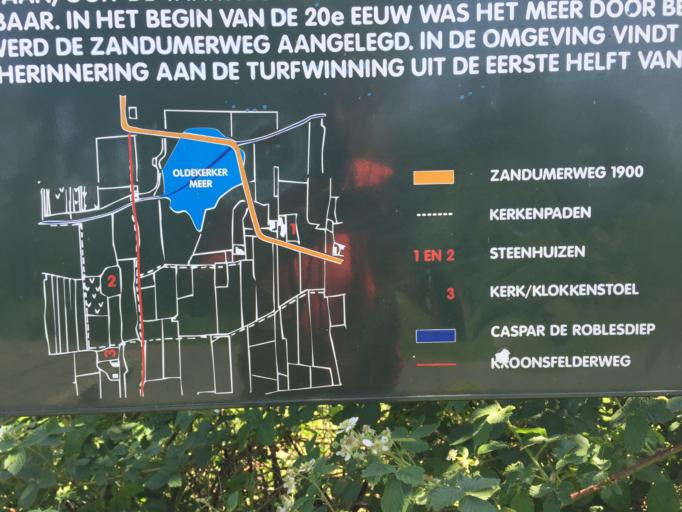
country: NL
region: Groningen
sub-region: Gemeente Zuidhorn
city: Grijpskerk
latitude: 53.2245
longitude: 6.3351
